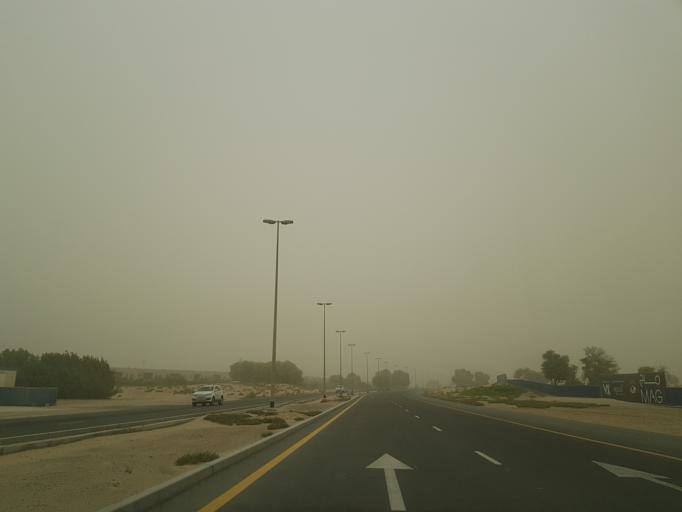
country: AE
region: Dubai
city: Dubai
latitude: 25.1470
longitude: 55.2864
